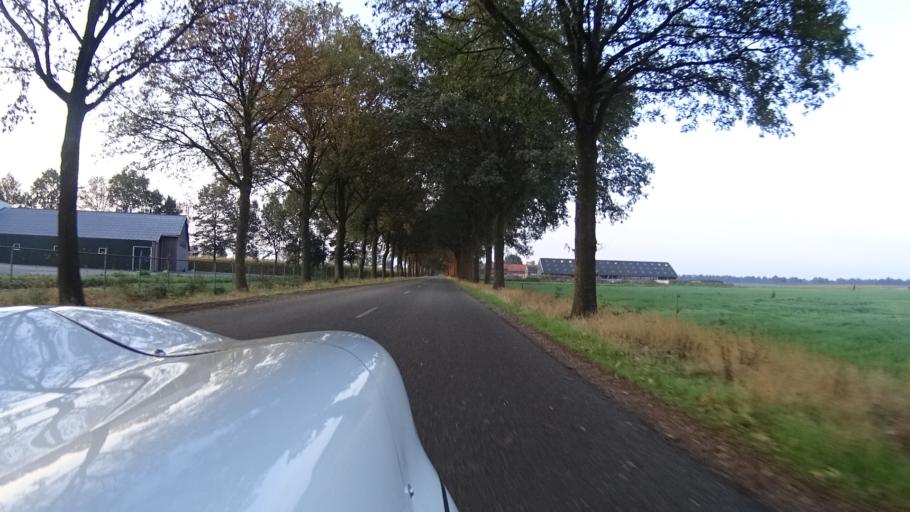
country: NL
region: North Brabant
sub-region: Gemeente Mill en Sint Hubert
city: Wilbertoord
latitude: 51.6152
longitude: 5.7810
